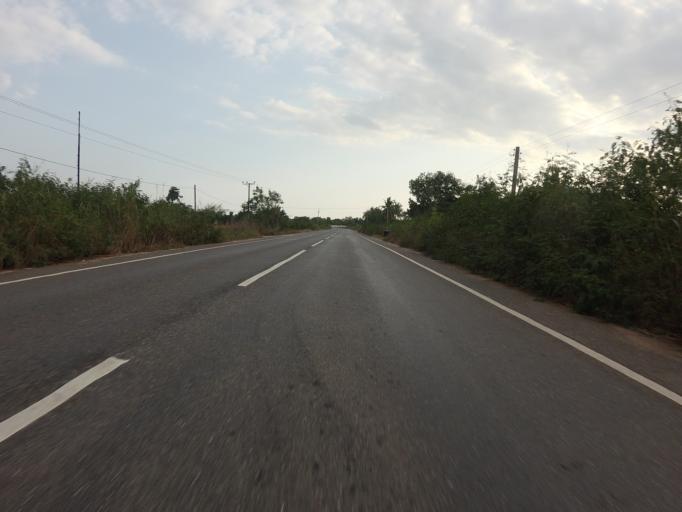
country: GH
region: Volta
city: Anloga
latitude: 6.0988
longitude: 0.5099
